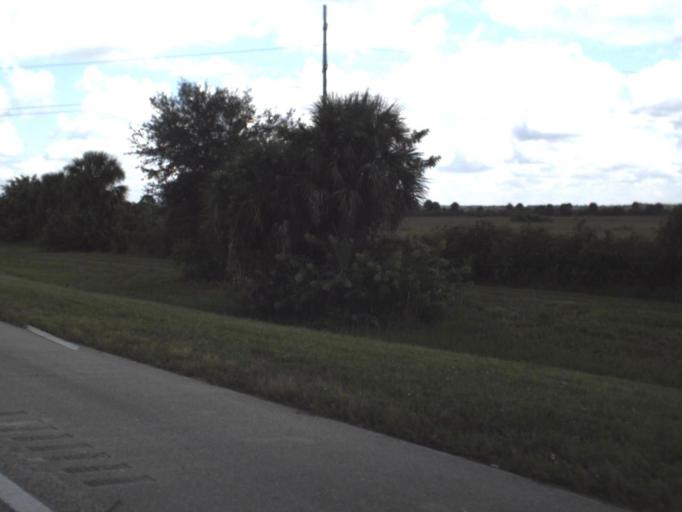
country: US
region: Florida
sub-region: Sarasota County
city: Laurel
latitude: 27.1857
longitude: -82.4424
